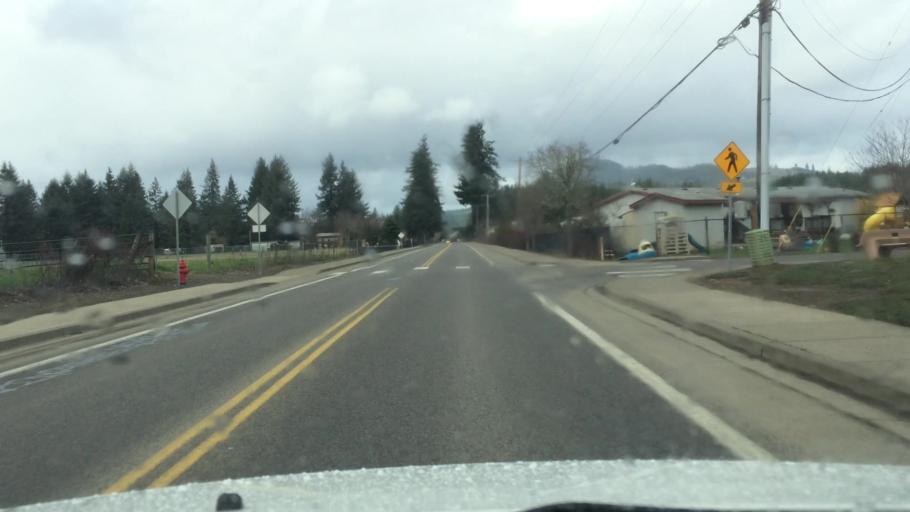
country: US
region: Oregon
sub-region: Polk County
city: Grand Ronde
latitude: 45.0668
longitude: -123.6119
